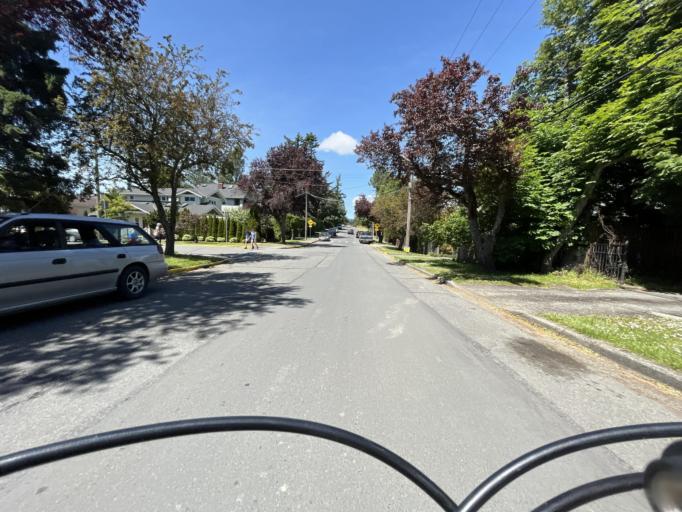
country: CA
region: British Columbia
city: Victoria
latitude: 48.4425
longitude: -123.3984
